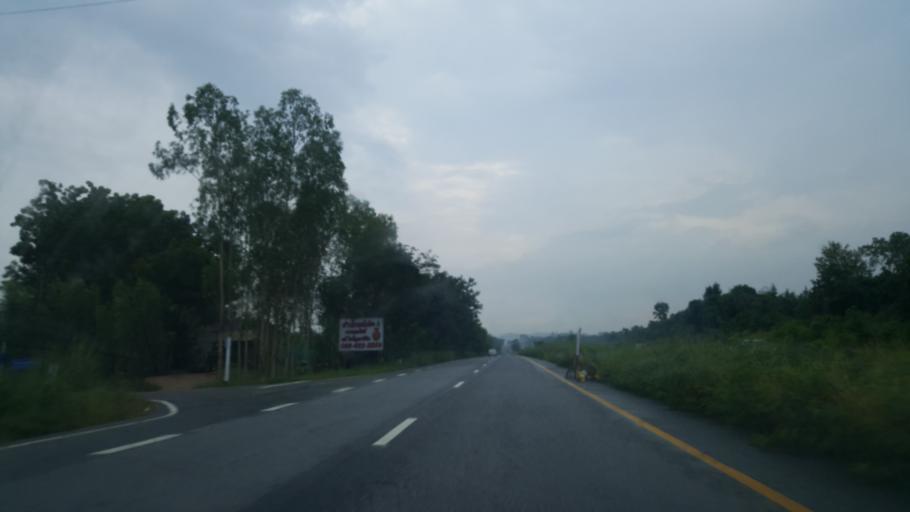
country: TH
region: Rayong
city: Ban Chang
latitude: 12.8428
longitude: 101.0126
